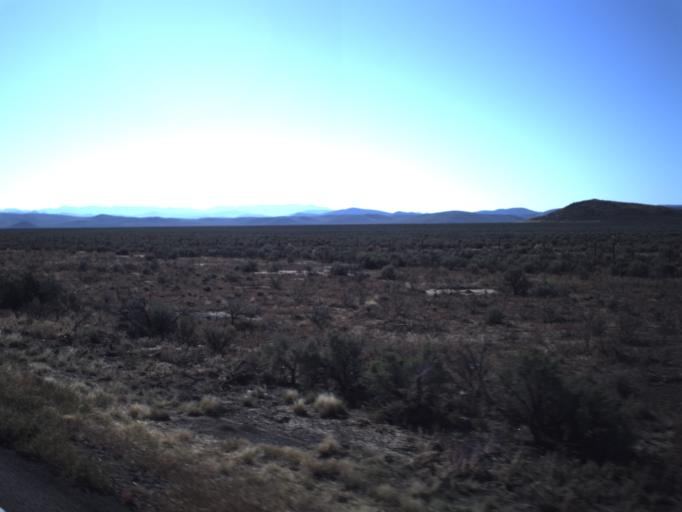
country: US
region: Utah
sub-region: Washington County
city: Enterprise
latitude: 37.7797
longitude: -113.8562
